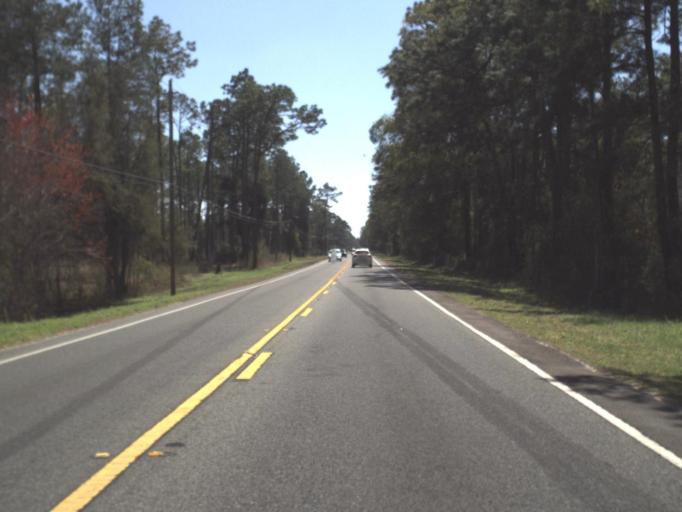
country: US
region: Florida
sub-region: Leon County
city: Woodville
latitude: 30.3465
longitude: -84.2574
